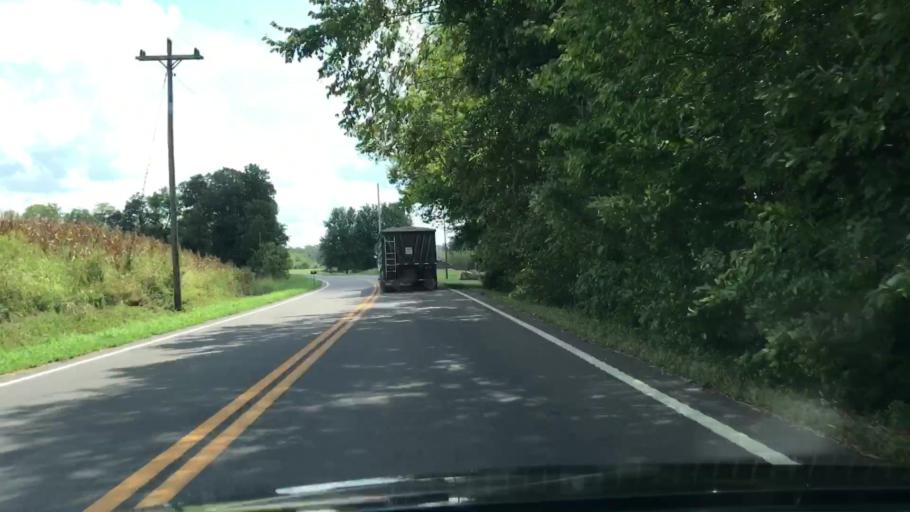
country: US
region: Tennessee
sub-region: Robertson County
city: Springfield
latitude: 36.6227
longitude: -86.9490
